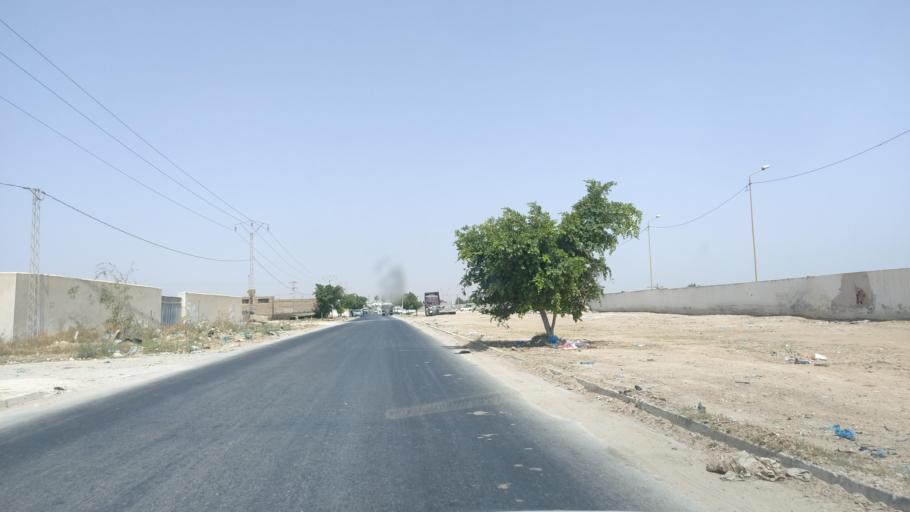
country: TN
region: Safaqis
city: Sfax
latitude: 34.6968
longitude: 10.7216
